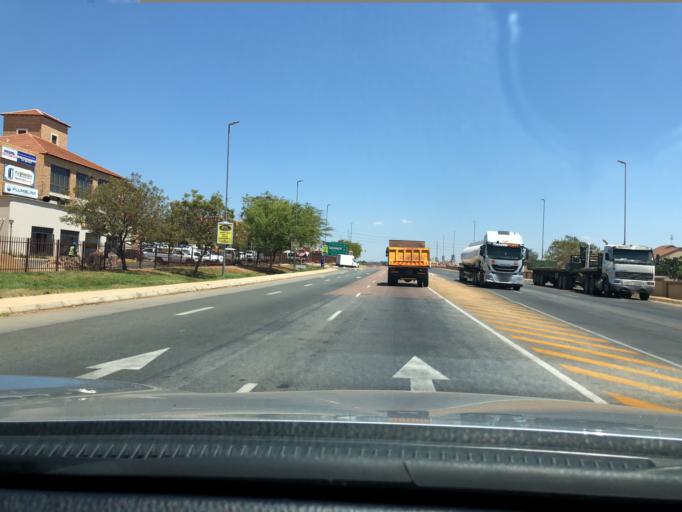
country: ZA
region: Limpopo
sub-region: Capricorn District Municipality
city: Polokwane
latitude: -23.8815
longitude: 29.5020
